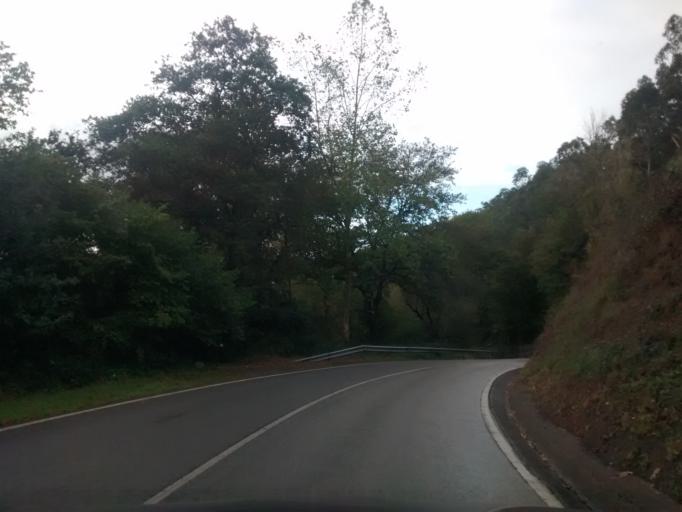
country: ES
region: Cantabria
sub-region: Provincia de Cantabria
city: Lierganes
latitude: 43.3496
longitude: -3.7258
